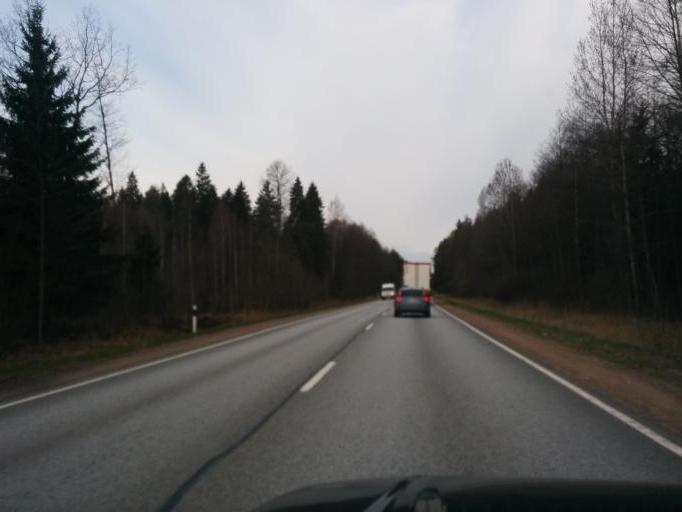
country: LV
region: Kekava
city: Balozi
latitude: 56.8251
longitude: 24.0666
